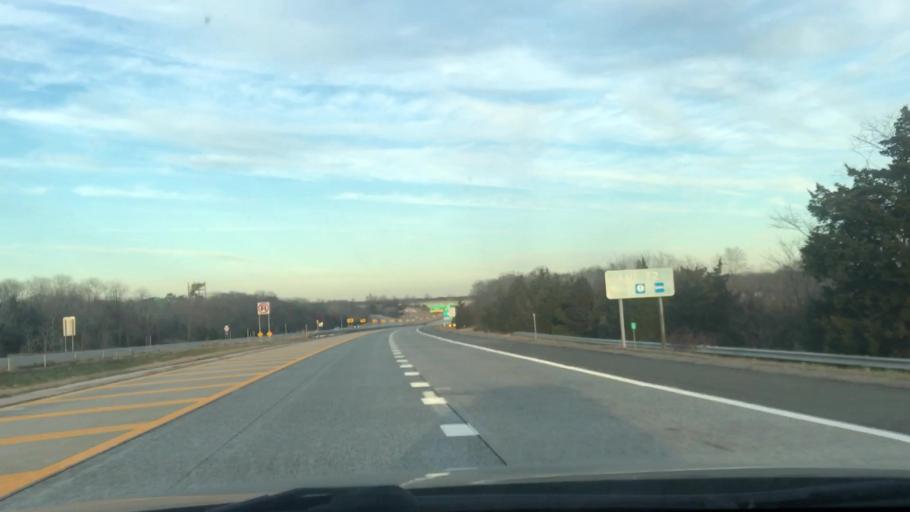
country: US
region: New York
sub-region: Suffolk County
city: Calverton
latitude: 40.9152
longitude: -72.7314
